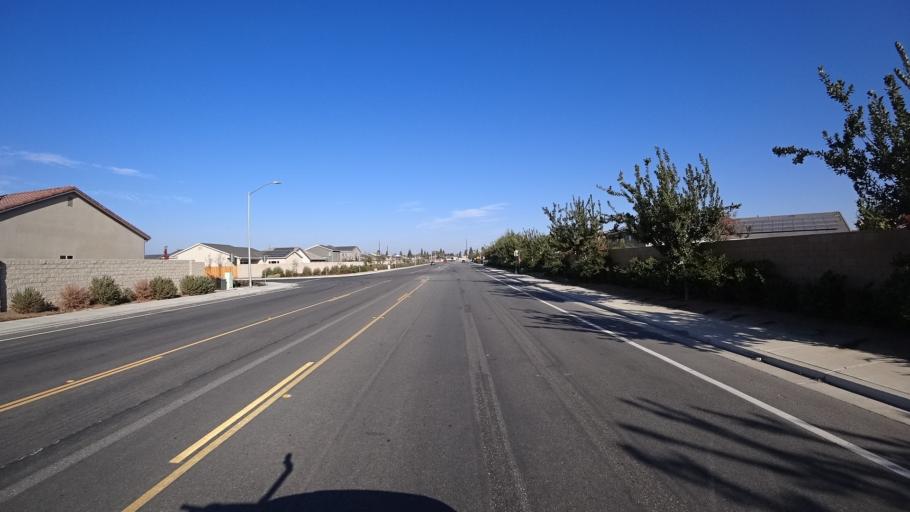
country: US
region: California
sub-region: Kern County
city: Greenfield
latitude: 35.2931
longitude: -119.0655
